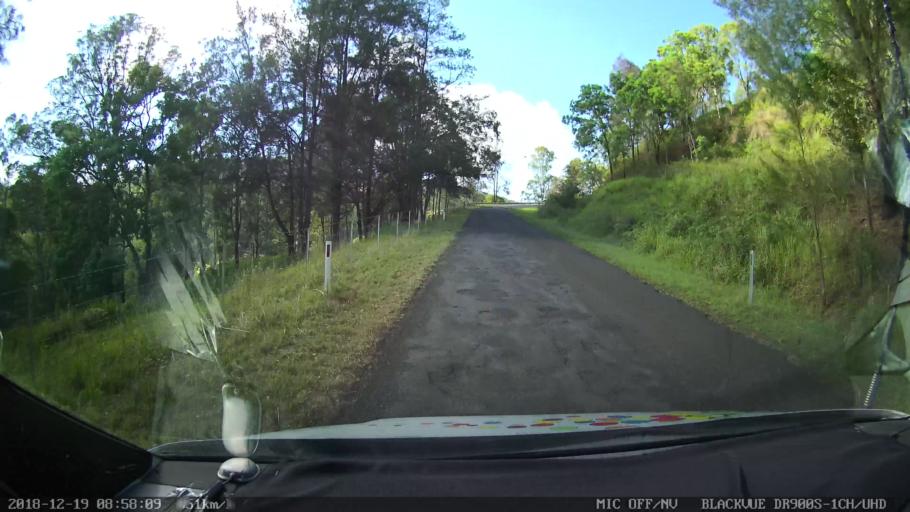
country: AU
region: New South Wales
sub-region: Kyogle
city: Kyogle
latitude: -28.4234
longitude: 152.9677
